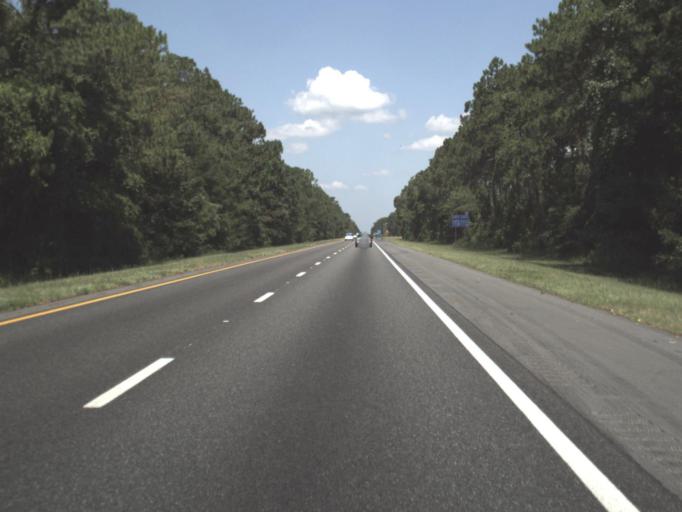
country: US
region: Florida
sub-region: Madison County
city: Madison
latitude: 30.3661
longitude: -83.2357
